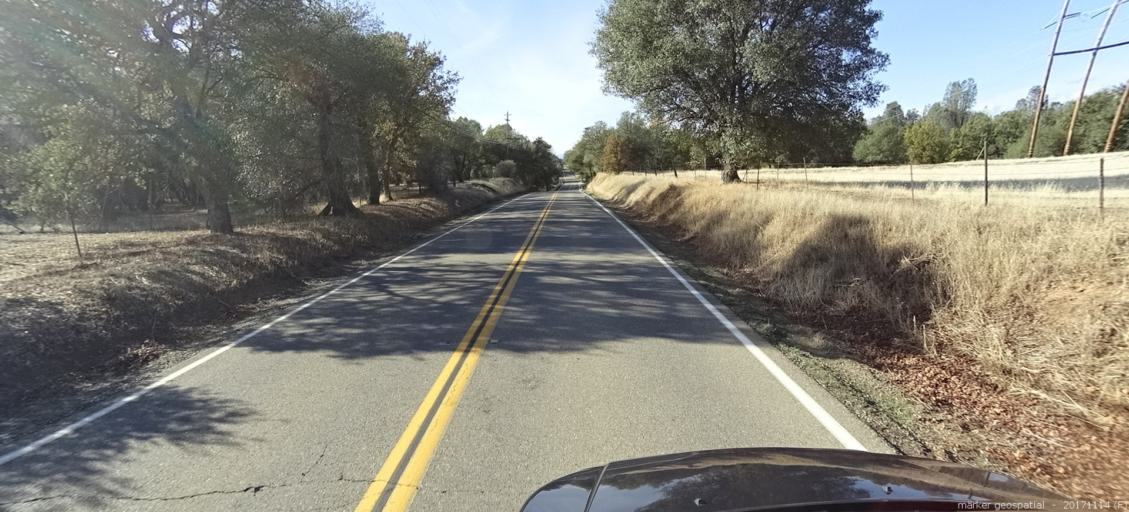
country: US
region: California
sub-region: Shasta County
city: Anderson
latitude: 40.3885
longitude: -122.4212
